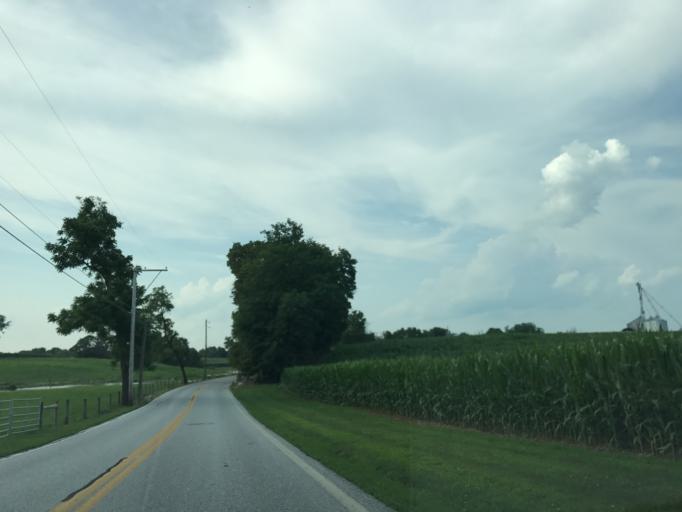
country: US
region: Pennsylvania
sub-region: Lancaster County
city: Mount Joy
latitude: 40.0999
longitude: -76.5345
